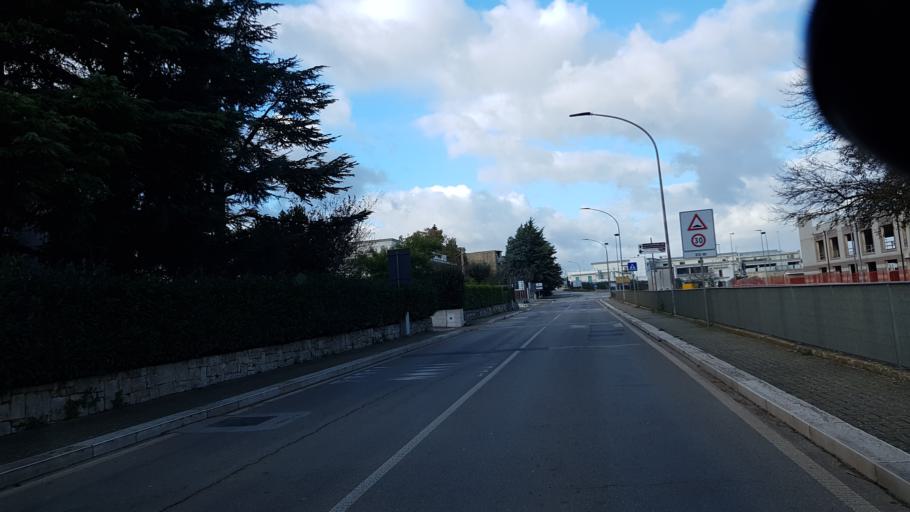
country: IT
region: Apulia
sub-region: Provincia di Bari
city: Alberobello
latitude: 40.7871
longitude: 17.2443
